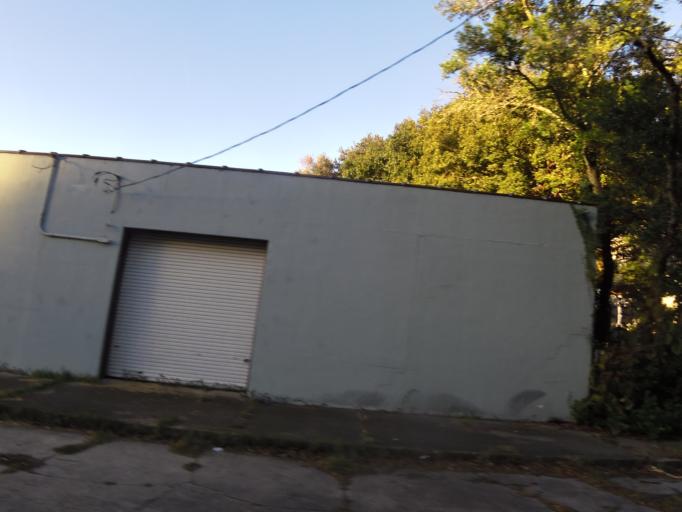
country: US
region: Florida
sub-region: Duval County
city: Jacksonville
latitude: 30.3426
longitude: -81.6478
